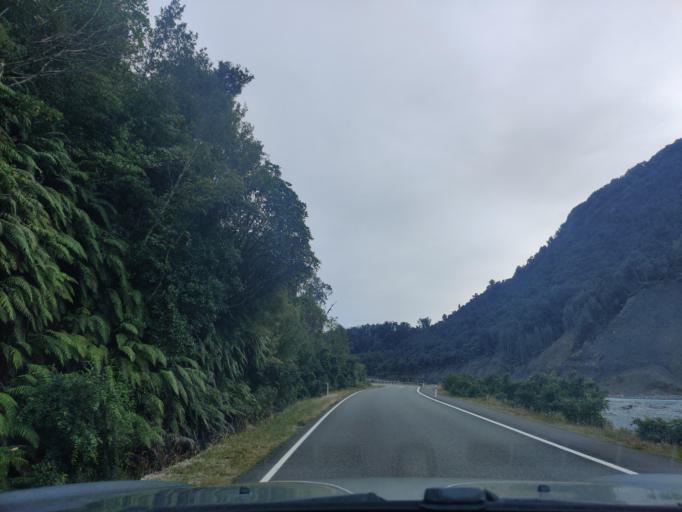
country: NZ
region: West Coast
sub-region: Westland District
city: Hokitika
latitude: -43.3988
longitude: 170.1808
